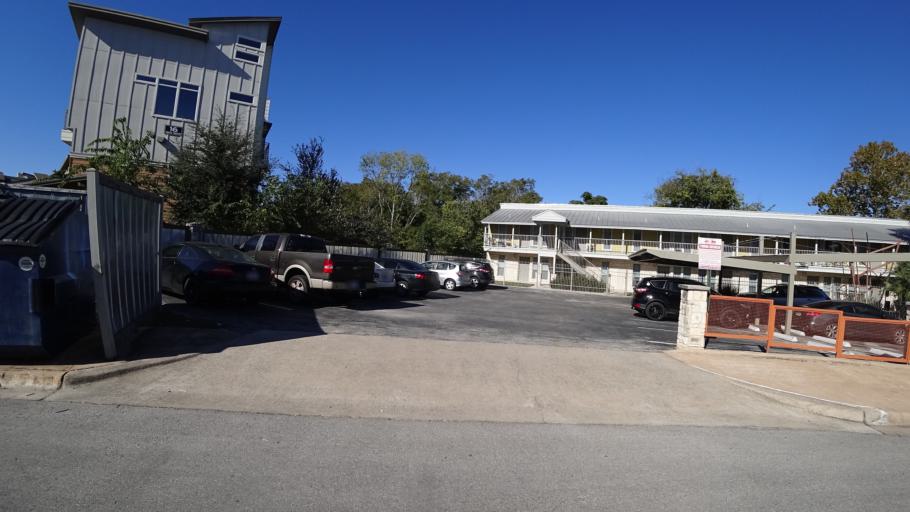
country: US
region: Texas
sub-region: Travis County
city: Austin
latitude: 30.2387
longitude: -97.7596
